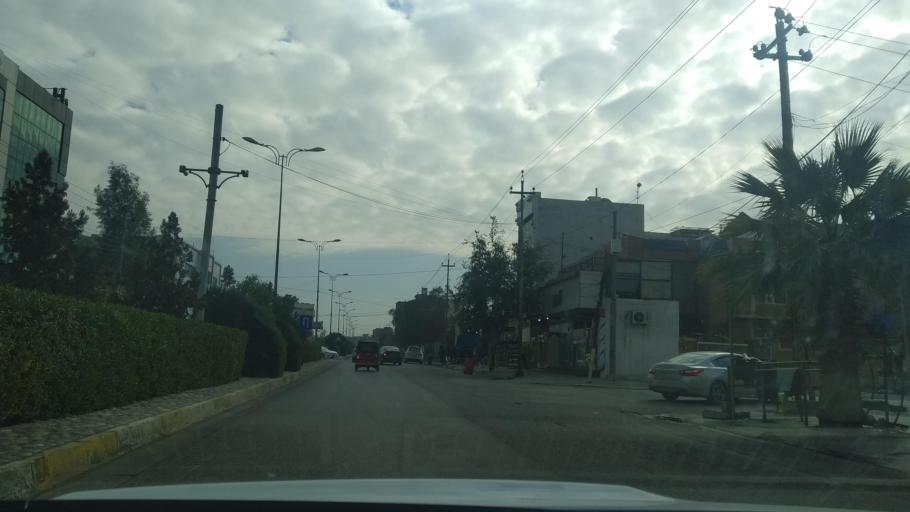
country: IQ
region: Arbil
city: Erbil
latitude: 36.1791
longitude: 44.0271
